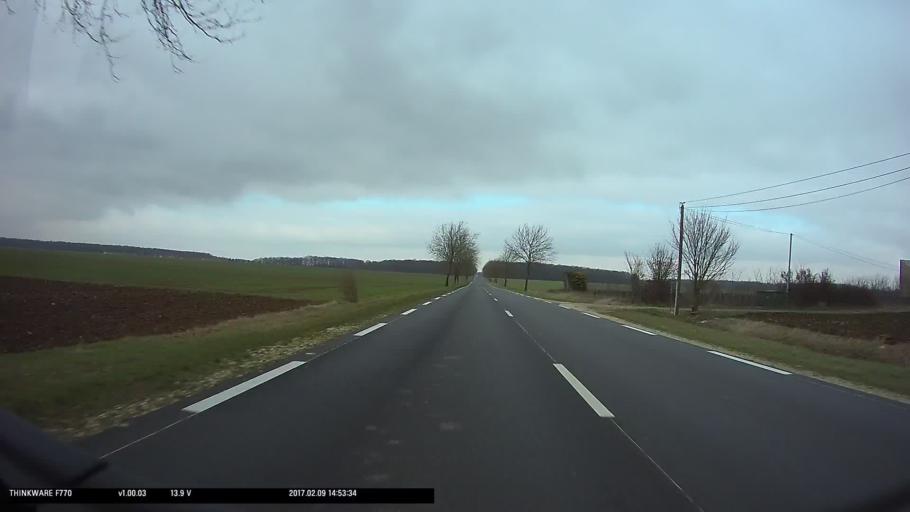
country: FR
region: Centre
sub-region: Departement du Cher
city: Levet
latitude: 46.9046
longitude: 2.4132
